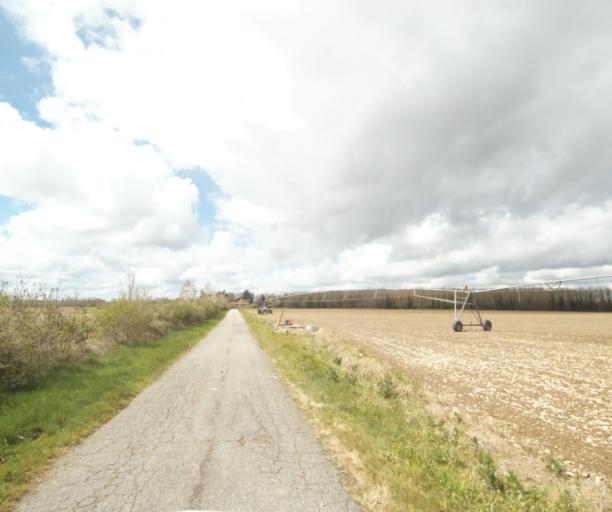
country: FR
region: Midi-Pyrenees
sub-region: Departement de la Haute-Garonne
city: Calmont
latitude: 43.2545
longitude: 1.6308
